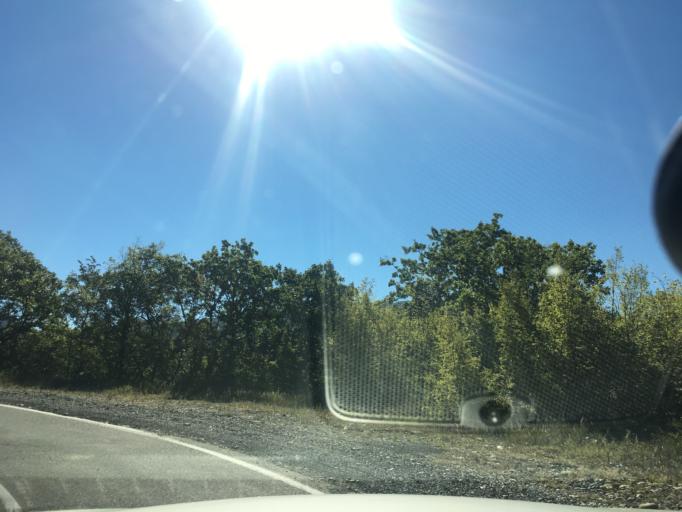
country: GE
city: Didi Lilo
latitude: 41.8643
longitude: 44.9165
